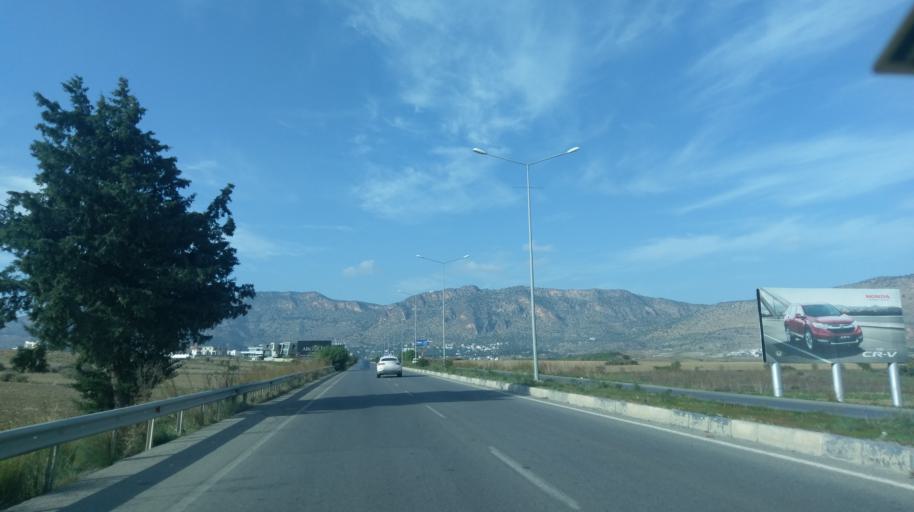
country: CY
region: Keryneia
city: Kyrenia
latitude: 35.2661
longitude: 33.2929
